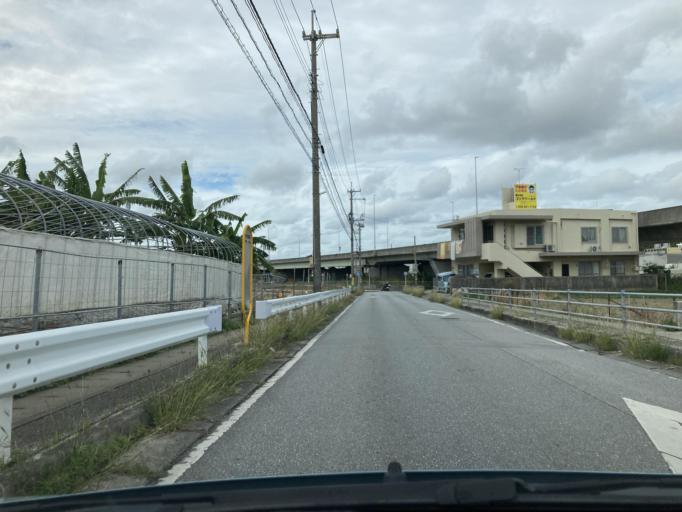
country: JP
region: Okinawa
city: Tomigusuku
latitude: 26.1747
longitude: 127.6740
